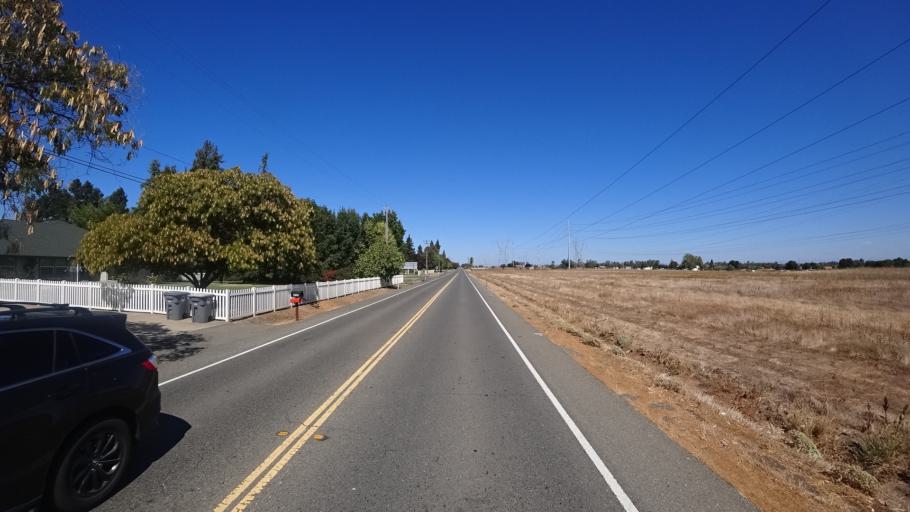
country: US
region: California
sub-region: Sacramento County
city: Vineyard
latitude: 38.4396
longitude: -121.3533
